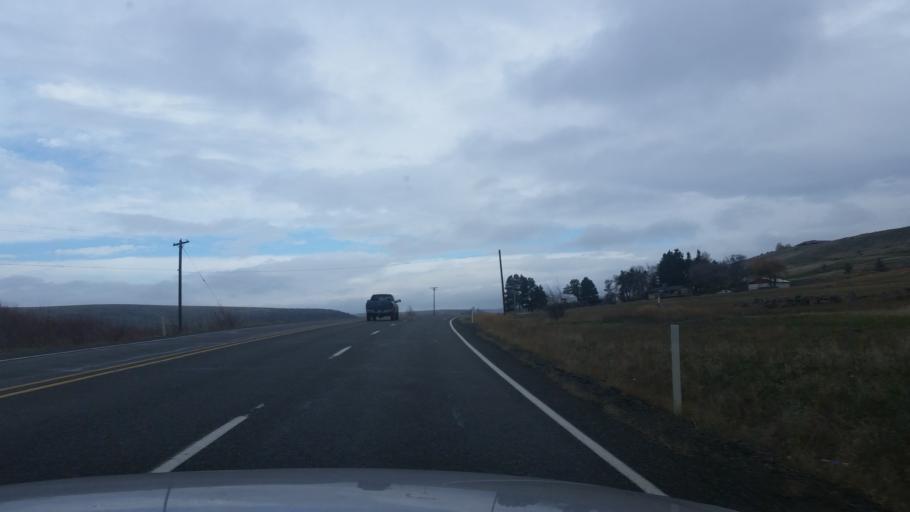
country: US
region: Washington
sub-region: Kittitas County
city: Ellensburg
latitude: 47.1043
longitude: -120.7064
